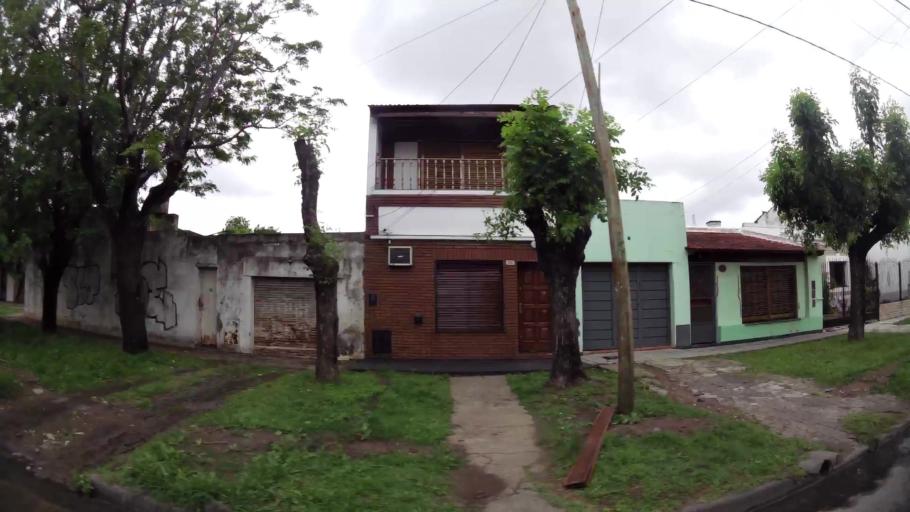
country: AR
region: Buenos Aires
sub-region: Partido de Lomas de Zamora
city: Lomas de Zamora
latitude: -34.7422
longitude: -58.3735
